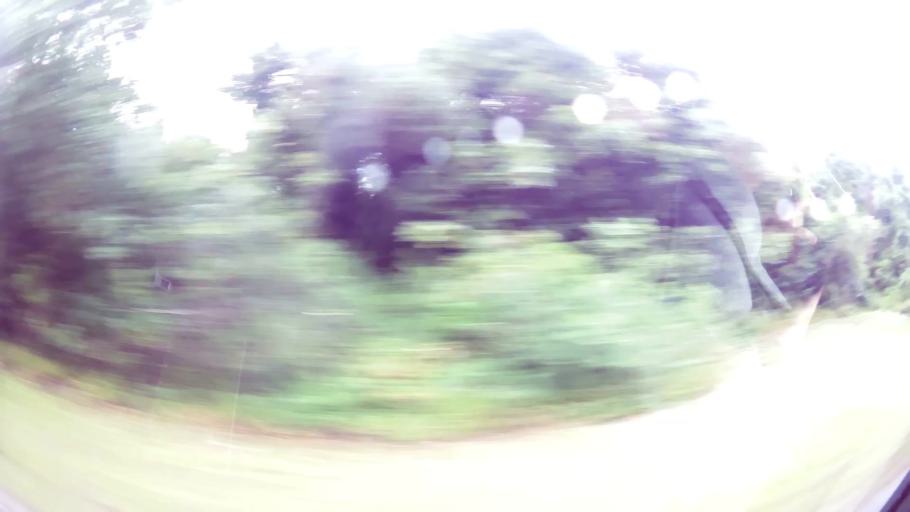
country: ZA
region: Eastern Cape
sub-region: Nelson Mandela Bay Metropolitan Municipality
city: Port Elizabeth
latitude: -34.0160
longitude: 25.5126
